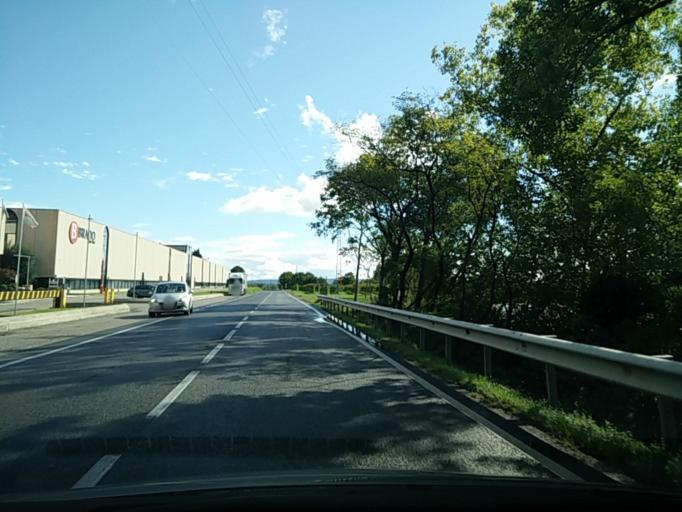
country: IT
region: Veneto
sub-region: Provincia di Treviso
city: Pederobba
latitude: 45.8956
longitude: 11.9561
